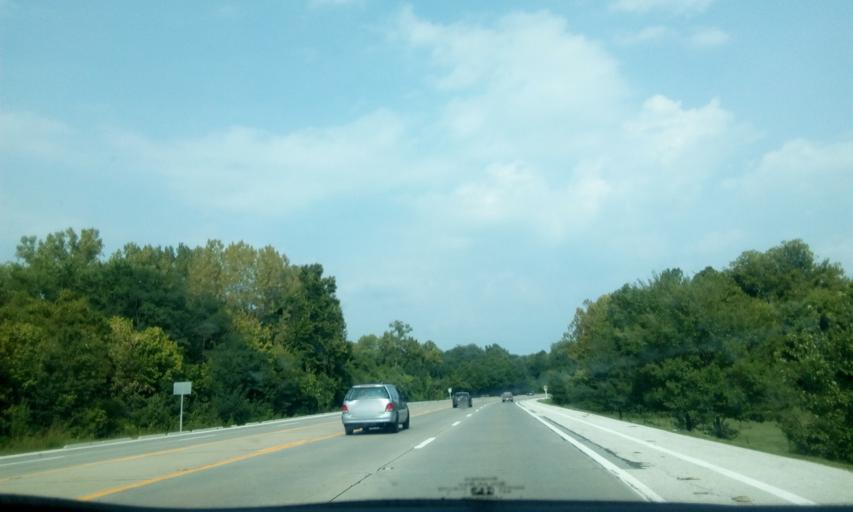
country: US
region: Missouri
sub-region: Saint Louis County
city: Town and Country
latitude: 38.5793
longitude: -90.4632
